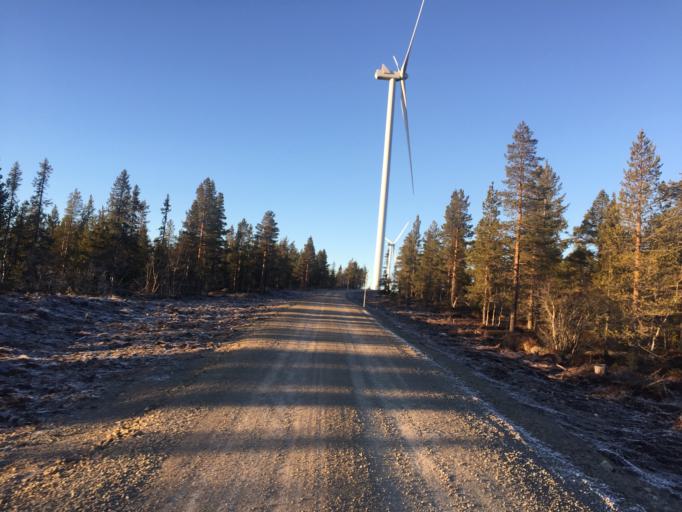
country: NO
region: Hedmark
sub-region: Elverum
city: Elverum
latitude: 61.2062
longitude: 11.7901
